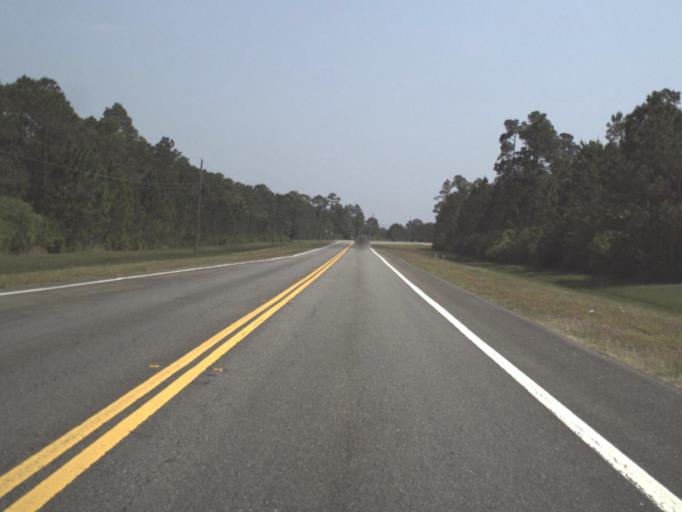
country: US
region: Florida
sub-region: Santa Rosa County
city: Bagdad
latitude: 30.5116
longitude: -87.0845
